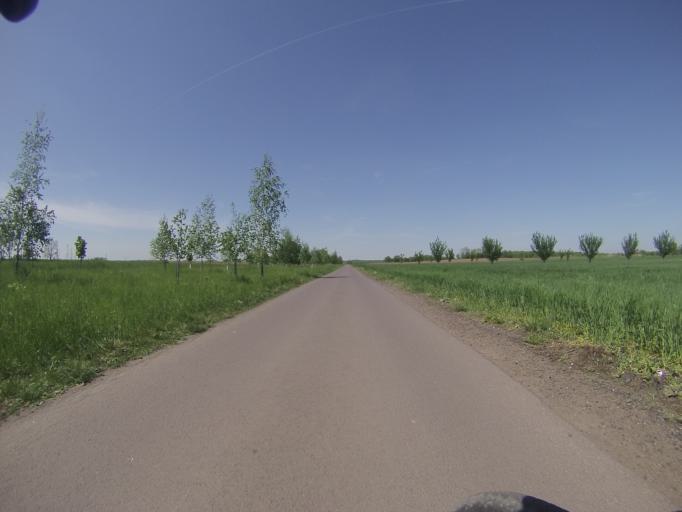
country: CZ
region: South Moravian
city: Novosedly
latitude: 48.8071
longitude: 16.4865
